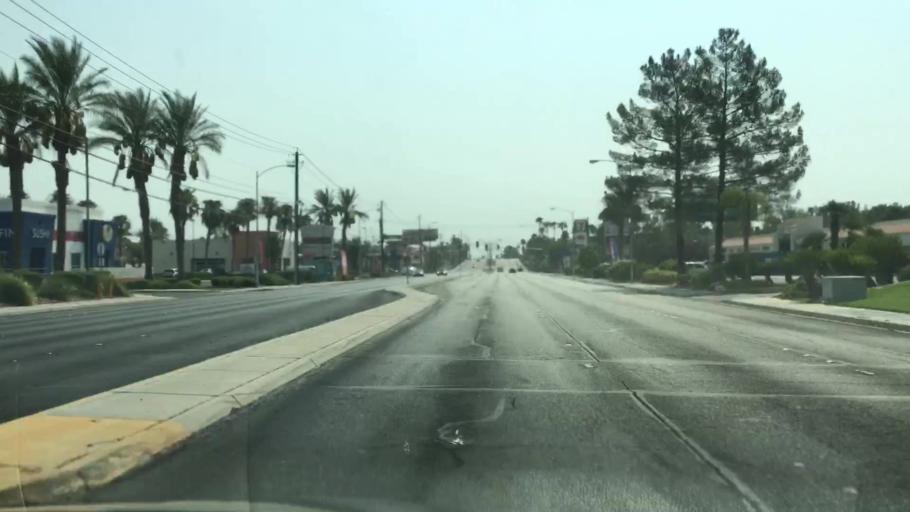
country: US
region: Nevada
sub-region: Clark County
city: Whitney
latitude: 36.0711
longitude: -115.0892
